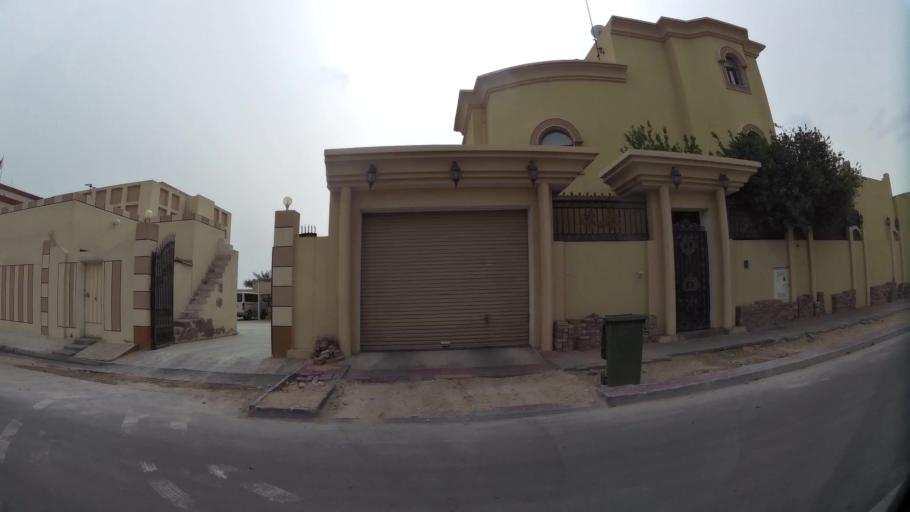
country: QA
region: Baladiyat ad Dawhah
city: Doha
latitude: 25.2434
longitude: 51.5169
